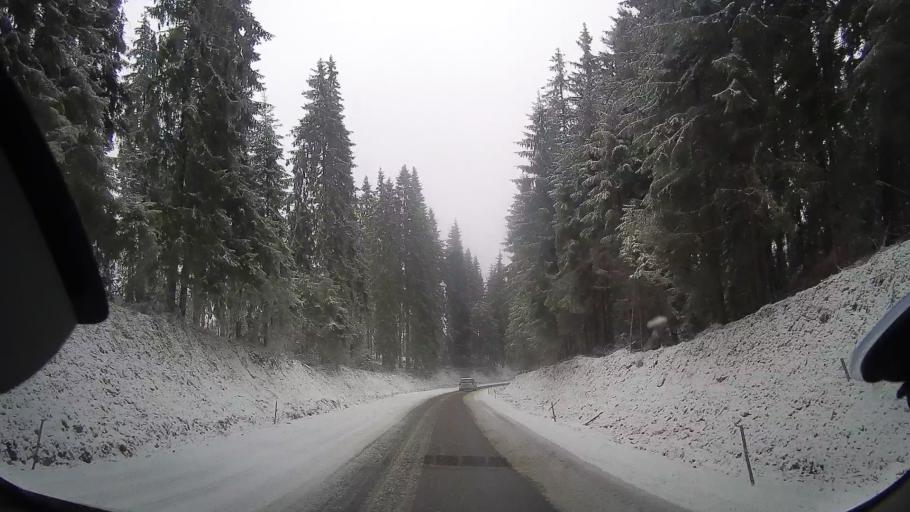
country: RO
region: Cluj
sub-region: Comuna Belis
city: Belis
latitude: 46.6381
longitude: 23.0417
